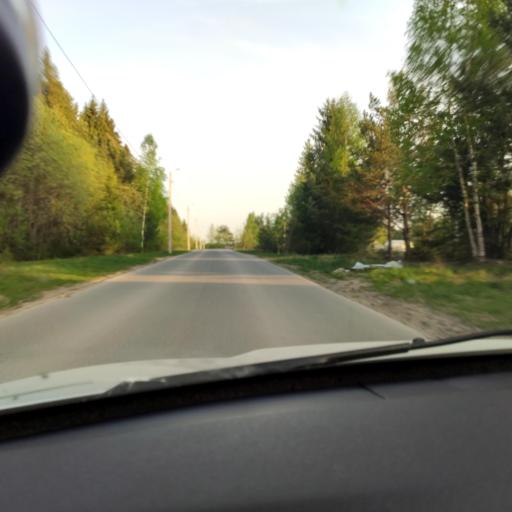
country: RU
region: Perm
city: Polazna
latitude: 58.2783
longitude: 56.4075
